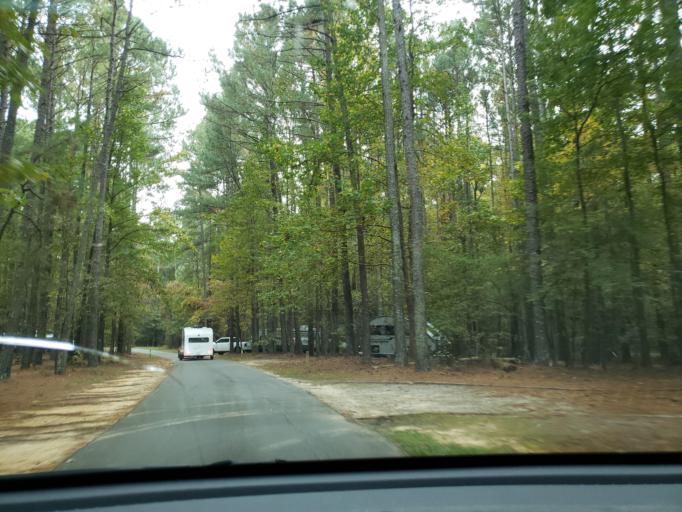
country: US
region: North Carolina
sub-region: Chatham County
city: Fearrington Village
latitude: 35.7429
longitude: -79.0362
